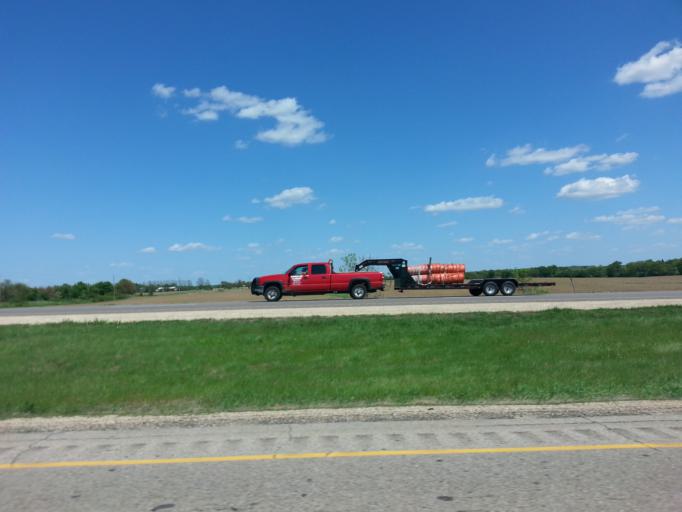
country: US
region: Wisconsin
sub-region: Rock County
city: Milton
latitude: 42.7846
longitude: -89.0046
